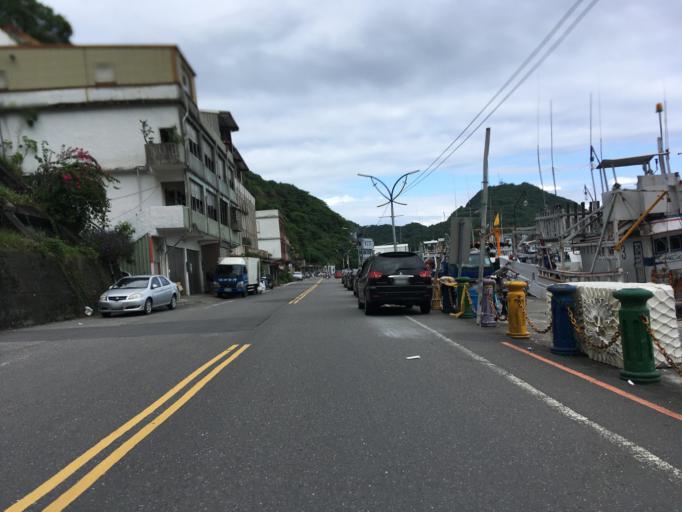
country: TW
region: Taiwan
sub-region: Yilan
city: Yilan
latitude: 24.5779
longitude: 121.8681
